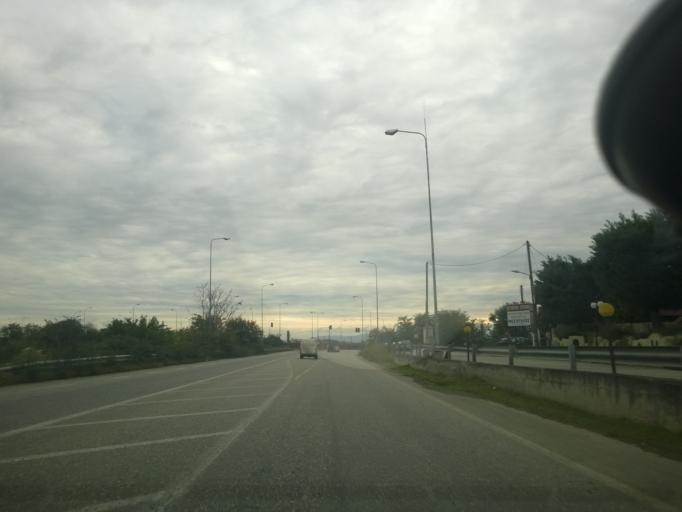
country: GR
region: Central Macedonia
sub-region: Nomos Pellis
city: Mavrovouni
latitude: 40.7893
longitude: 22.1593
